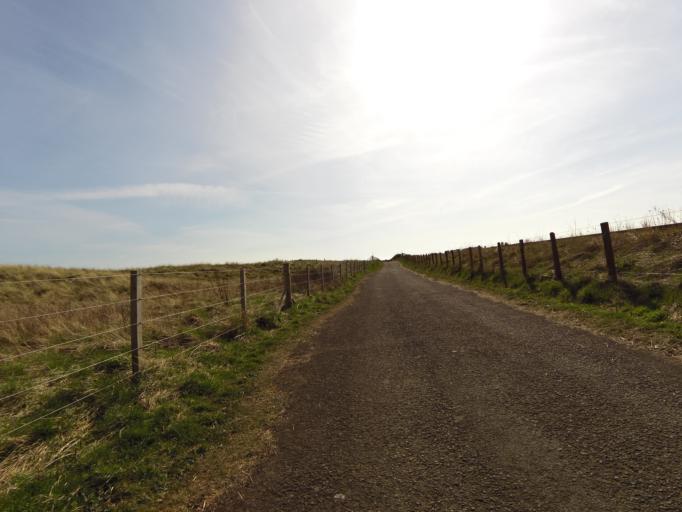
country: GB
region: Scotland
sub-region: Angus
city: Arbroath
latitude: 56.5373
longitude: -2.6277
